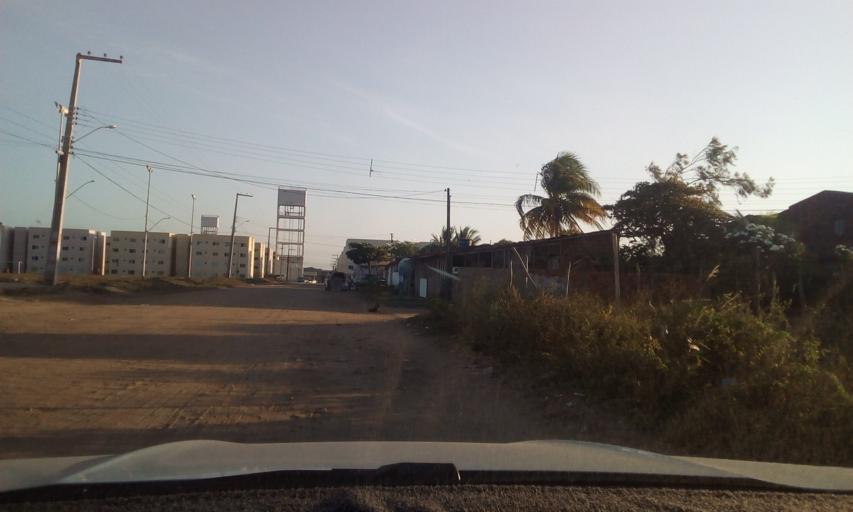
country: BR
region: Paraiba
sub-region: Bayeux
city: Bayeux
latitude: -7.1811
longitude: -34.9313
